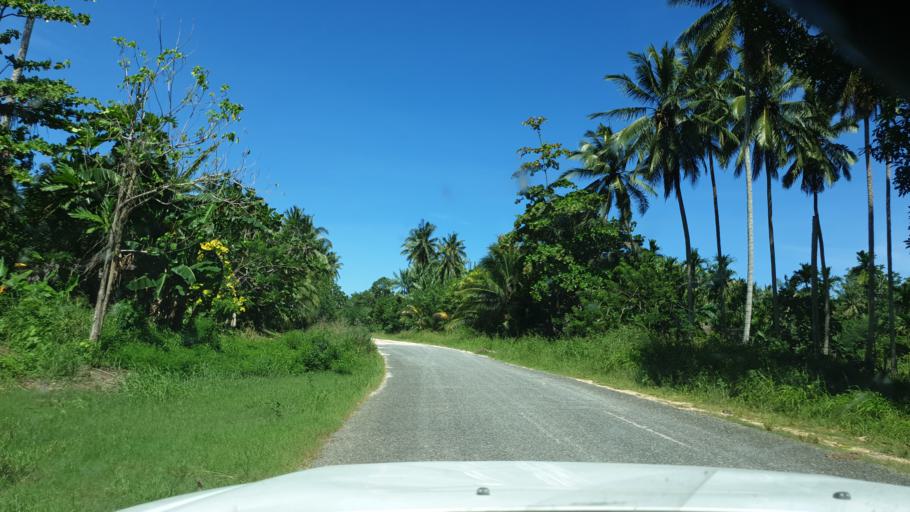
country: PG
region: Madang
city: Madang
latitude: -4.4585
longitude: 145.3947
